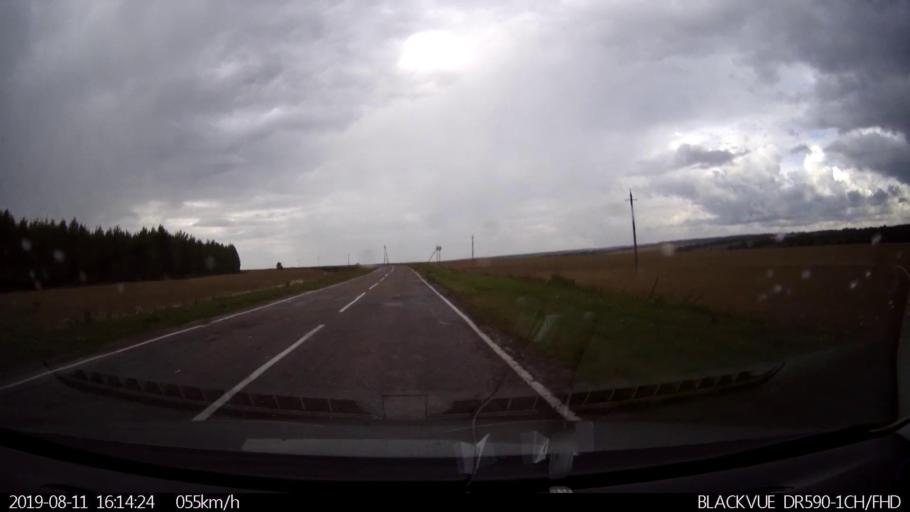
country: RU
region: Ulyanovsk
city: Ignatovka
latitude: 54.0278
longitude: 47.6341
